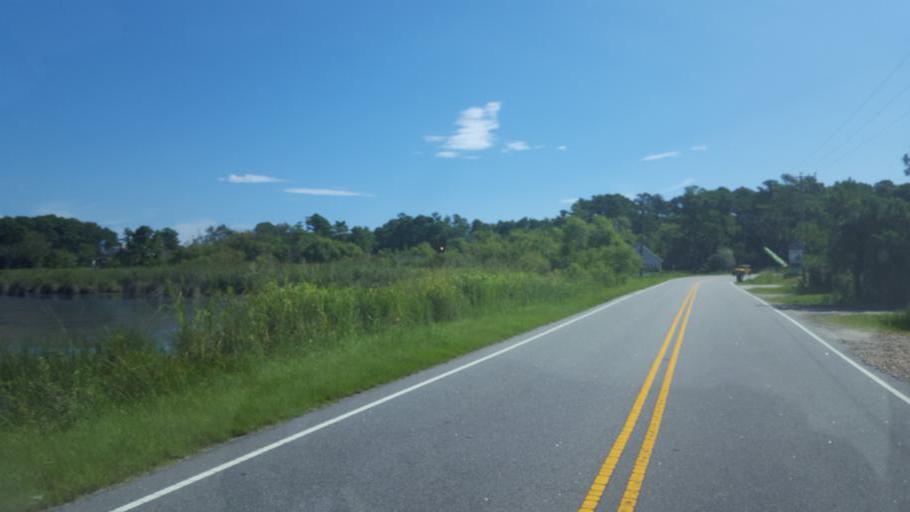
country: US
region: North Carolina
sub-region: Dare County
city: Kill Devil Hills
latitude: 36.0142
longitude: -75.6805
